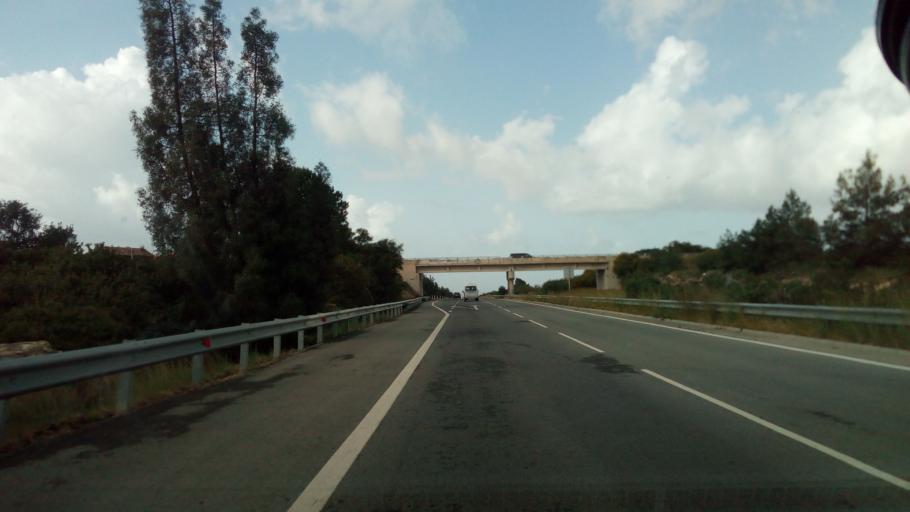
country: CY
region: Larnaka
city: Kolossi
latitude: 34.6870
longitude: 32.9394
